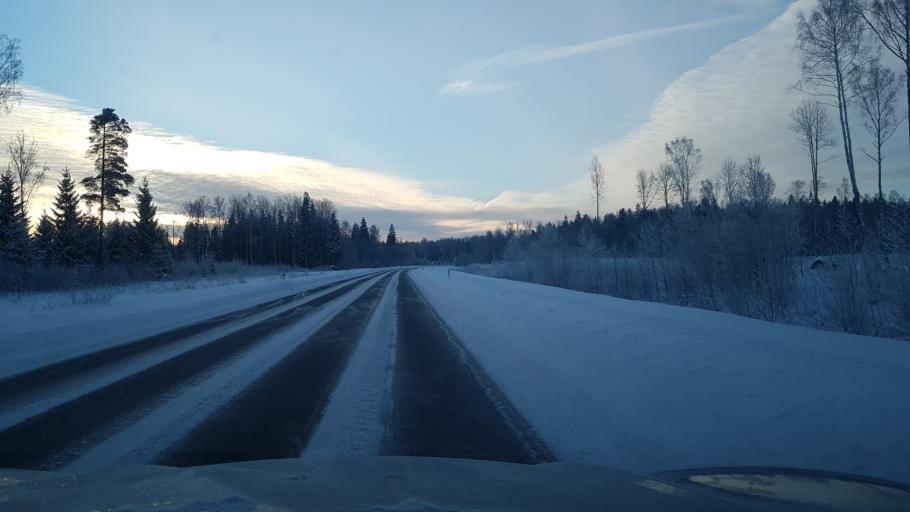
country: EE
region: Ida-Virumaa
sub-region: Johvi vald
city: Johvi
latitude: 59.3548
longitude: 27.4658
